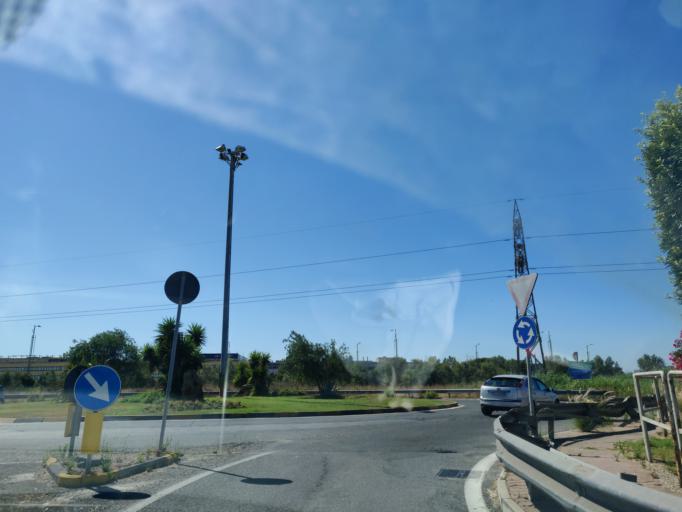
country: IT
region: Latium
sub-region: Citta metropolitana di Roma Capitale
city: Npp 23 (Parco Leonardo)
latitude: 41.8079
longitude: 12.3024
